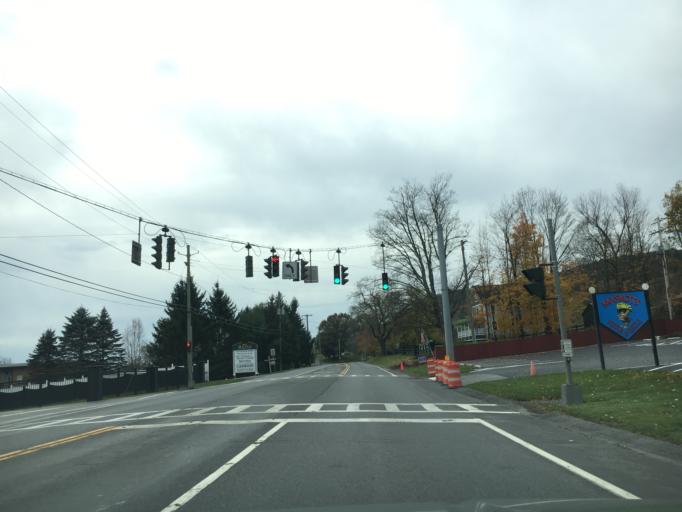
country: US
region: New York
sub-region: Otsego County
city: Cooperstown
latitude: 42.6392
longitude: -74.9655
